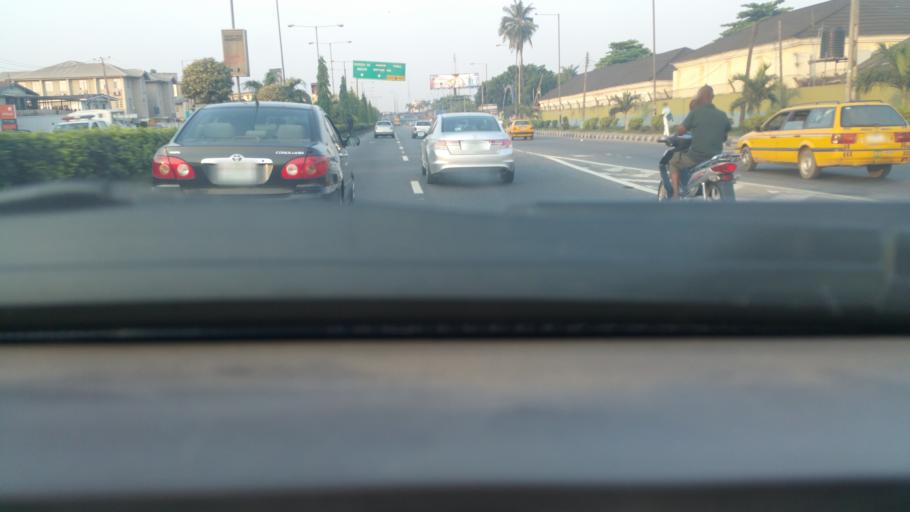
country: NG
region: Lagos
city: Surulere
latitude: 6.5121
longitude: 3.3639
